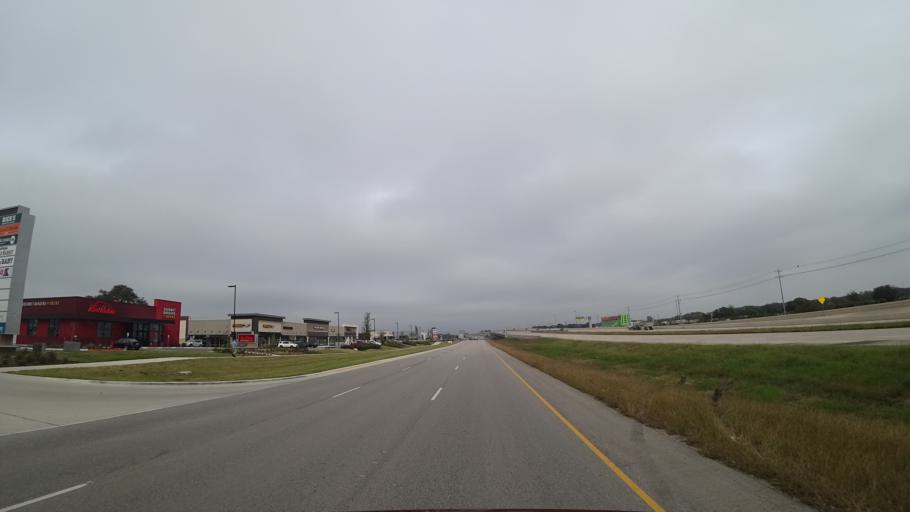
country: US
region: Texas
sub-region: Williamson County
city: Cedar Park
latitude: 30.5323
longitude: -97.8175
